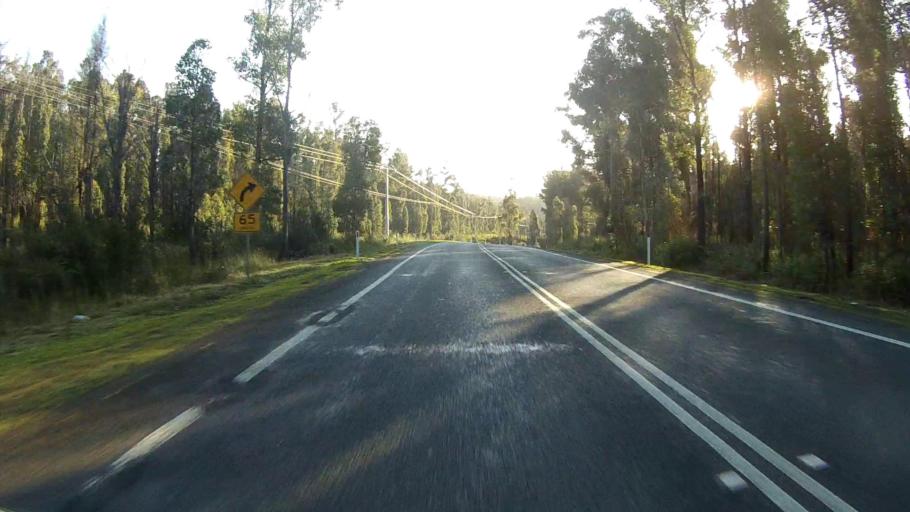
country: AU
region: Tasmania
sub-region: Sorell
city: Sorell
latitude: -42.9865
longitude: 147.9184
